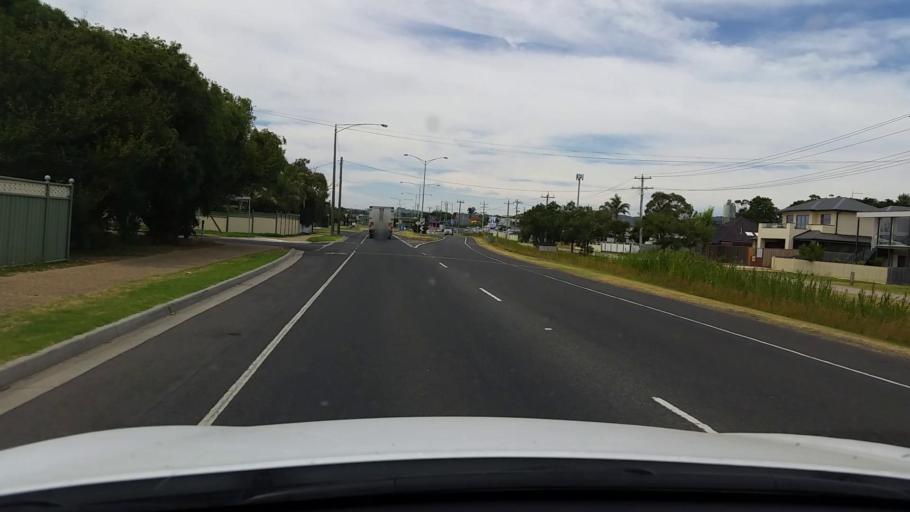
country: AU
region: Victoria
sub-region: Mornington Peninsula
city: Dromana
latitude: -38.3290
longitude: 144.9822
